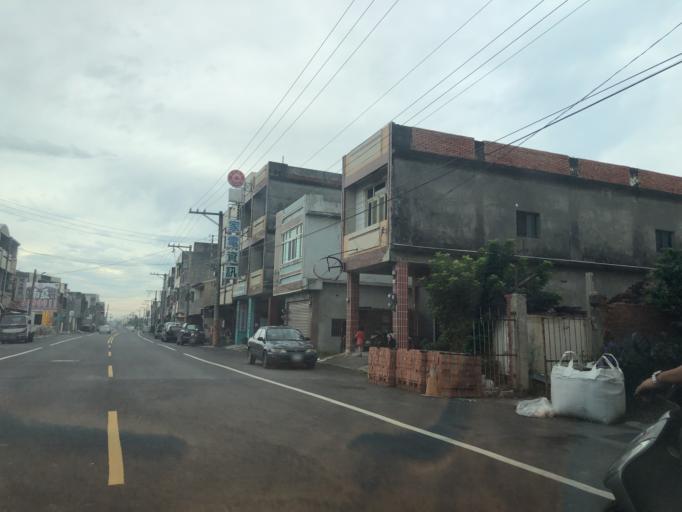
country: TW
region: Taiwan
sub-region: Chiayi
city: Taibao
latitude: 23.7028
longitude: 120.2001
